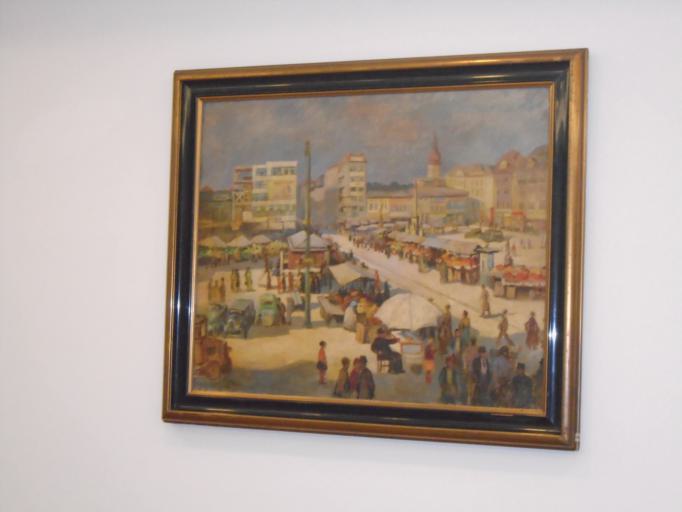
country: CZ
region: Moravskoslezsky
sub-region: Okres Ostrava-Mesto
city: Ostrava
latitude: 49.8286
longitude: 18.2669
